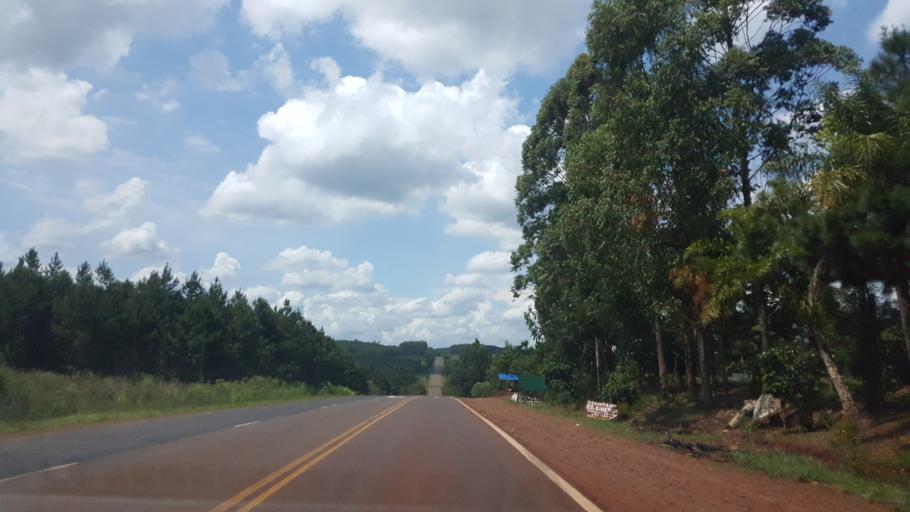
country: AR
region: Misiones
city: Garuhape
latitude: -26.8111
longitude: -54.9347
